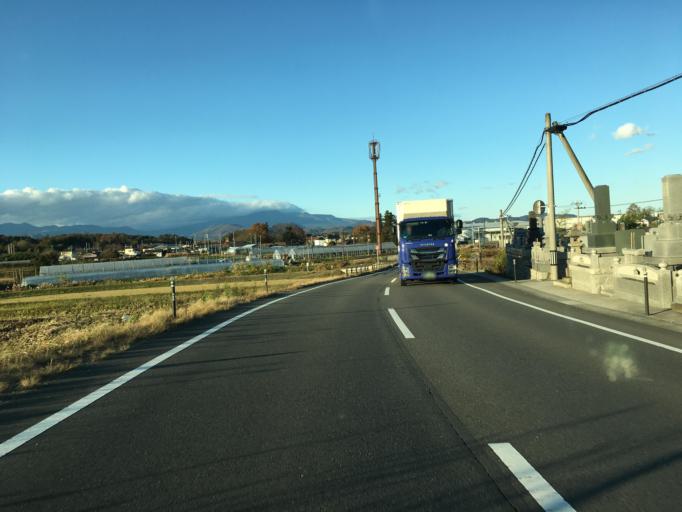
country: JP
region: Fukushima
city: Koriyama
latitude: 37.4155
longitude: 140.3065
